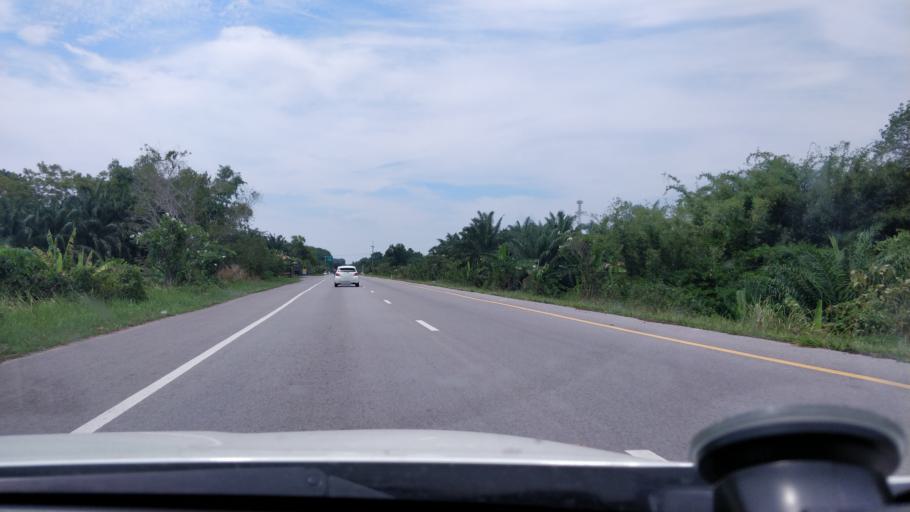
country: TH
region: Surat Thani
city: Khian Sa
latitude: 8.7827
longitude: 99.1614
